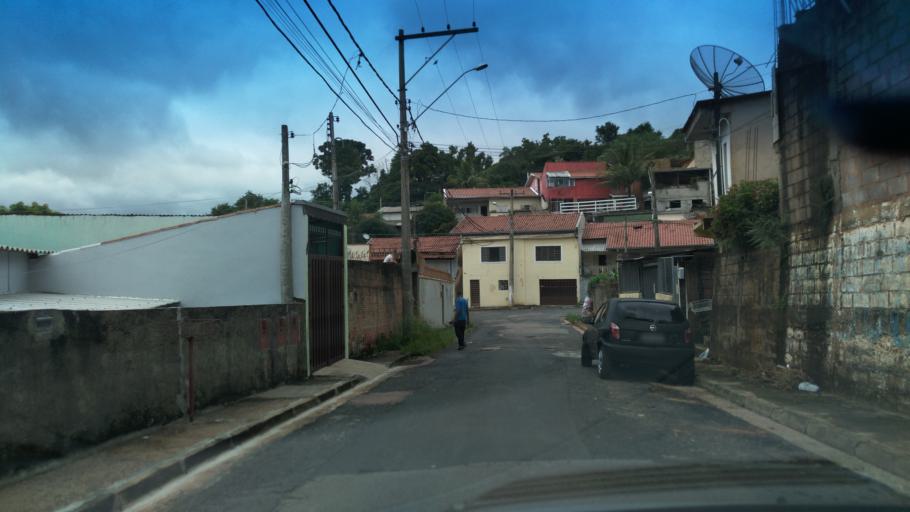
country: BR
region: Sao Paulo
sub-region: Valinhos
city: Valinhos
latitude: -22.9597
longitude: -47.0038
